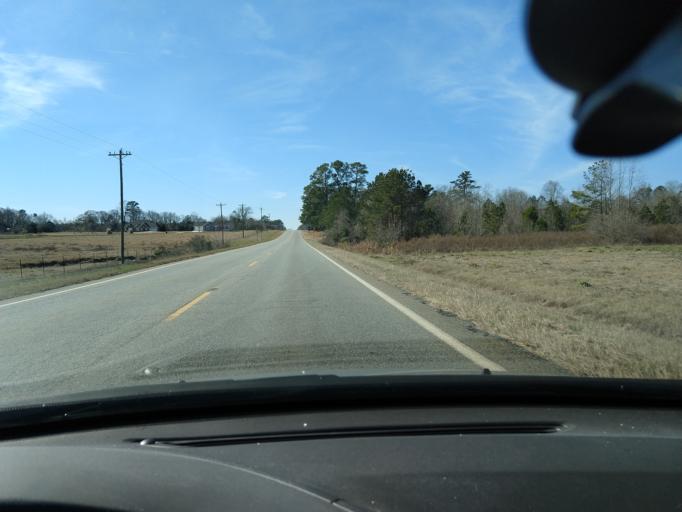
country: US
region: Georgia
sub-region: Dooly County
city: Unadilla
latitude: 32.3406
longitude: -83.7960
